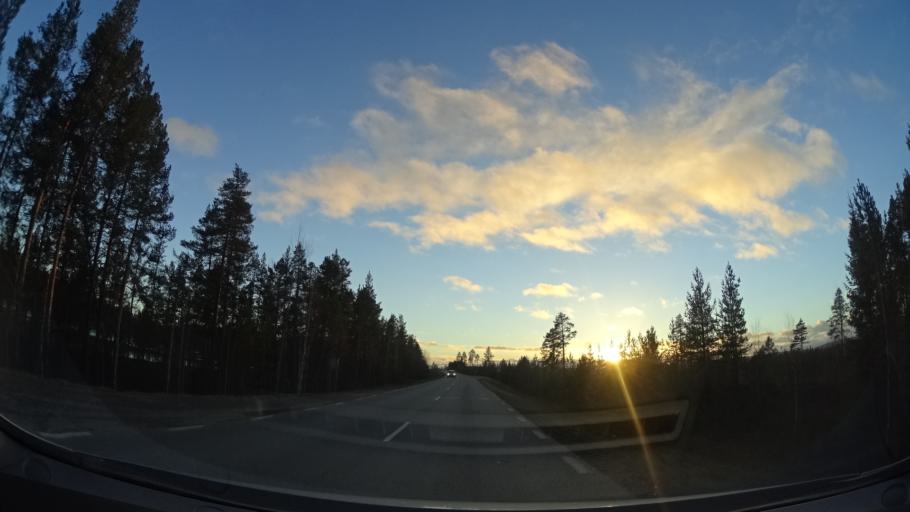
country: SE
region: Jaemtland
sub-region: Stroemsunds Kommun
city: Stroemsund
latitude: 63.9860
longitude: 15.5005
